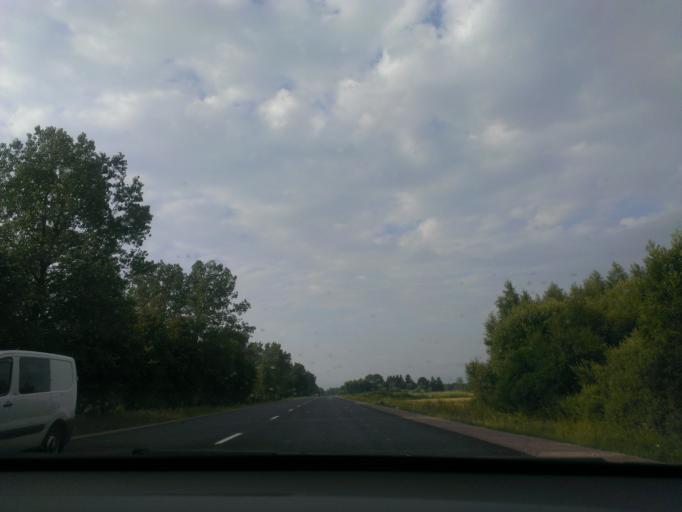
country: LV
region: Lecava
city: Iecava
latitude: 56.6751
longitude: 24.2365
